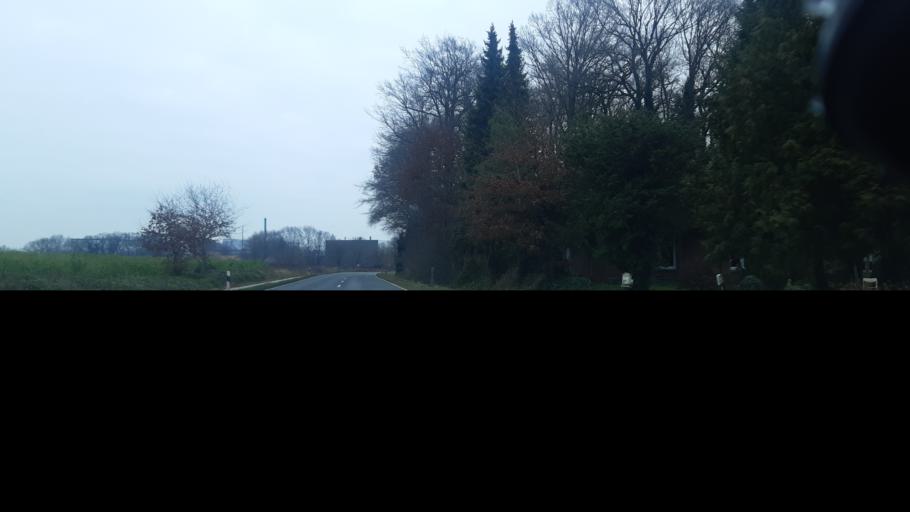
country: DE
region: Lower Saxony
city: Essen
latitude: 52.7272
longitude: 8.0229
